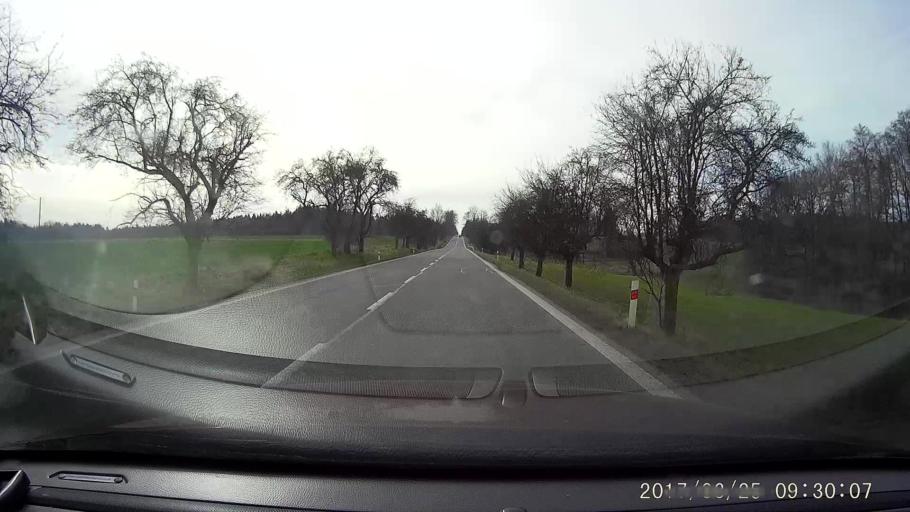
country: PL
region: Silesian Voivodeship
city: Zawidow
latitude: 51.0073
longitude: 15.0696
